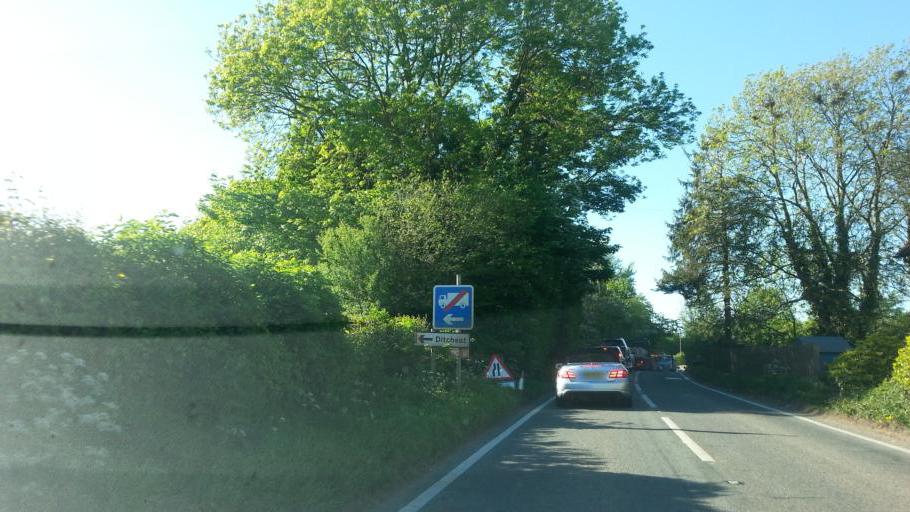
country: GB
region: England
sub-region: Somerset
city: Castle Cary
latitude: 51.1199
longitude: -2.5179
